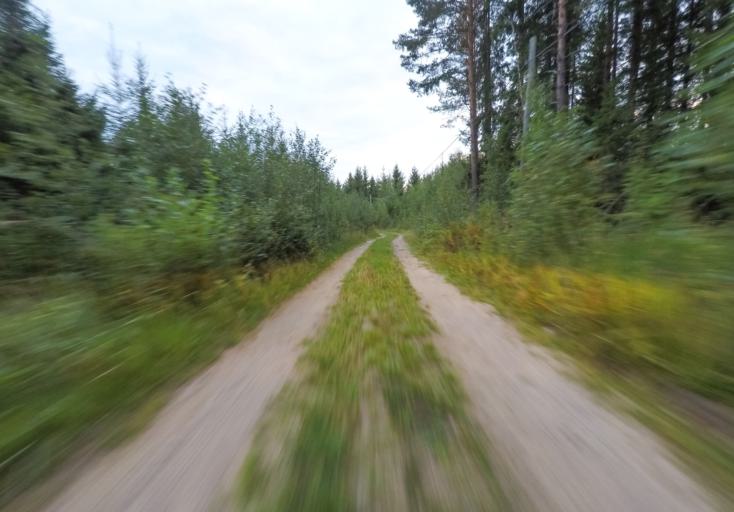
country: FI
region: Central Finland
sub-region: Jyvaeskylae
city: Hankasalmi
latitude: 62.4246
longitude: 26.6651
